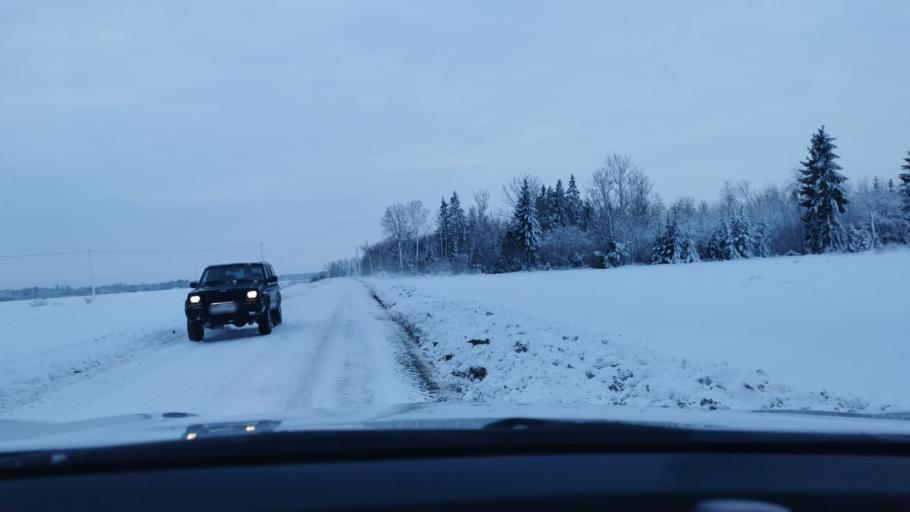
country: EE
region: Laeaene-Virumaa
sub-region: Viru-Nigula vald
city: Kunda
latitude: 59.4877
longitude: 26.4066
